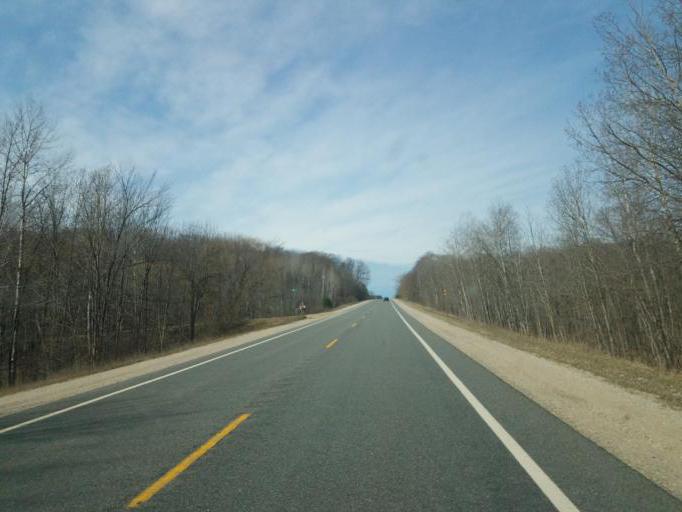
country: US
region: Michigan
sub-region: Oceana County
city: Shelby
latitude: 43.5707
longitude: -86.2194
